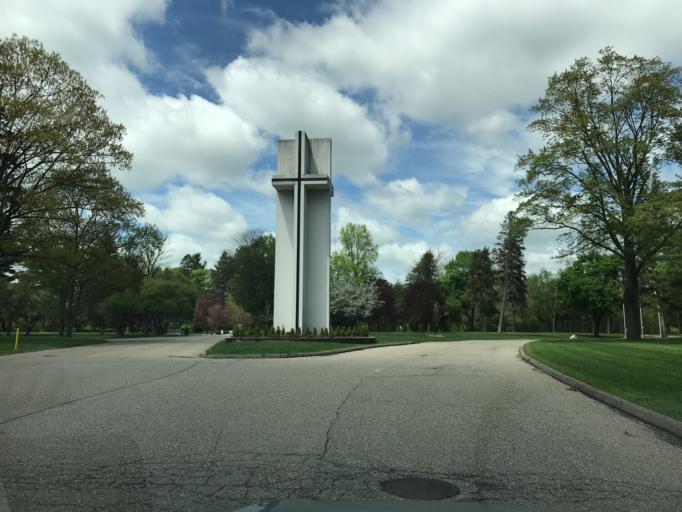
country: US
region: Michigan
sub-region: Oakland County
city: Franklin
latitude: 42.4718
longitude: -83.2992
